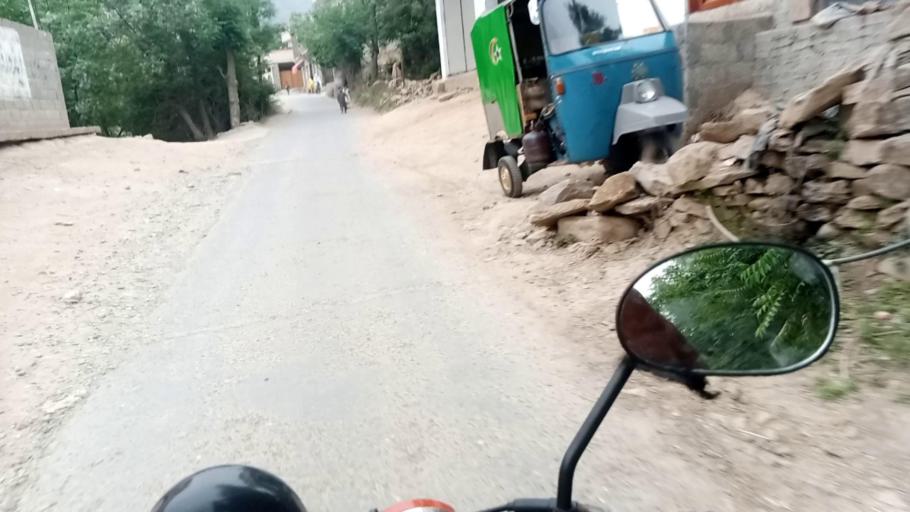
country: PK
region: Khyber Pakhtunkhwa
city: Saidu Sharif
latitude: 34.7543
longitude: 72.3783
